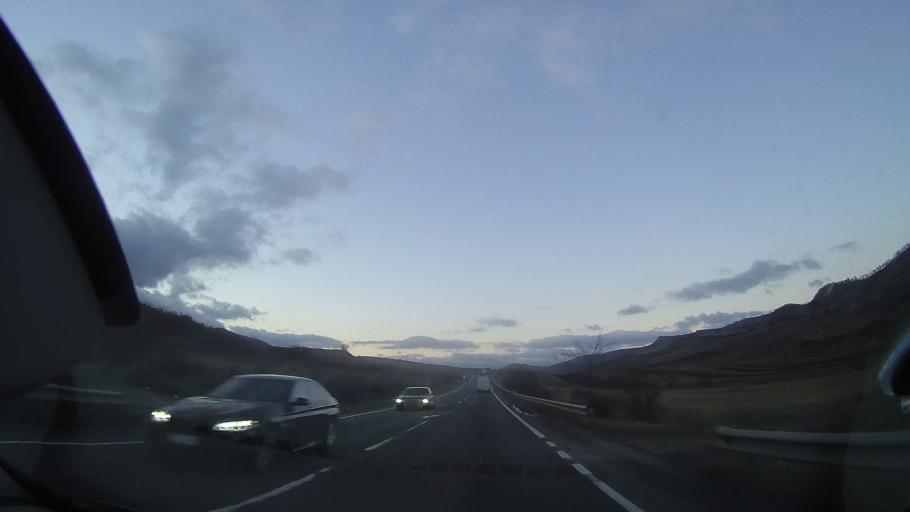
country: RO
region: Cluj
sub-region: Comuna Capusu Mare
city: Capusu Mare
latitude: 46.8054
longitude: 23.2595
